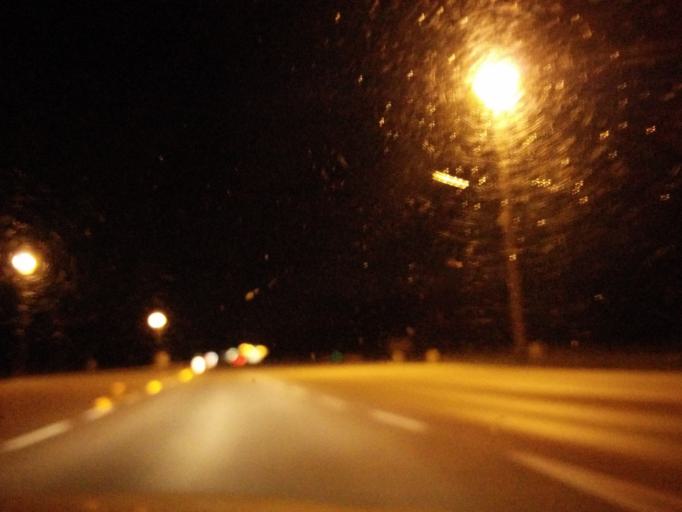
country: HR
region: Vukovarsko-Srijemska
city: Nijemci
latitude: 45.0468
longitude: 19.0238
